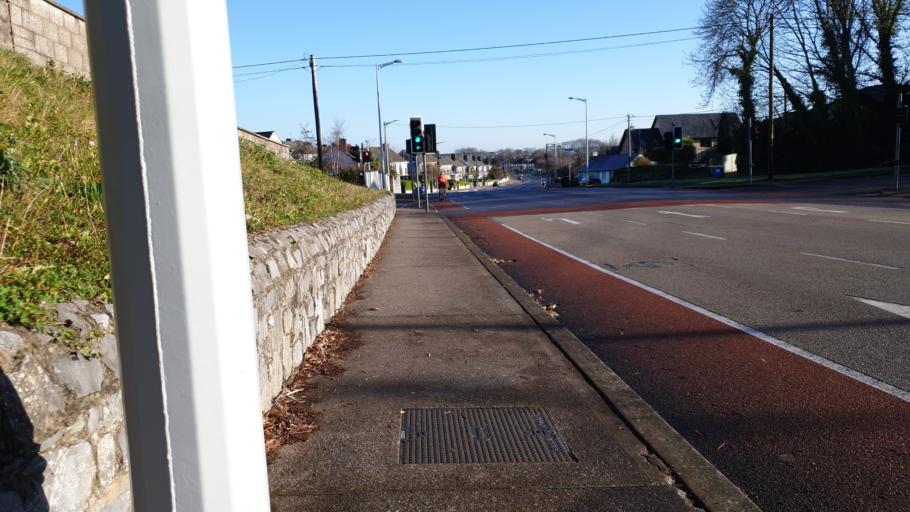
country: IE
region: Munster
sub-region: County Cork
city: Cork
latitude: 51.8867
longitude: -8.4290
